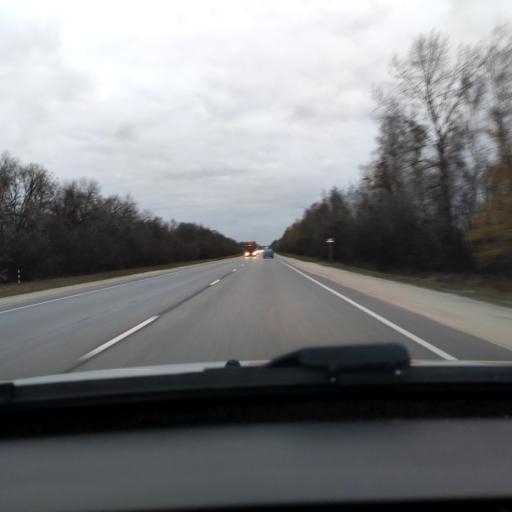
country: RU
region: Lipetsk
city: Borinskoye
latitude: 52.3996
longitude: 39.2368
